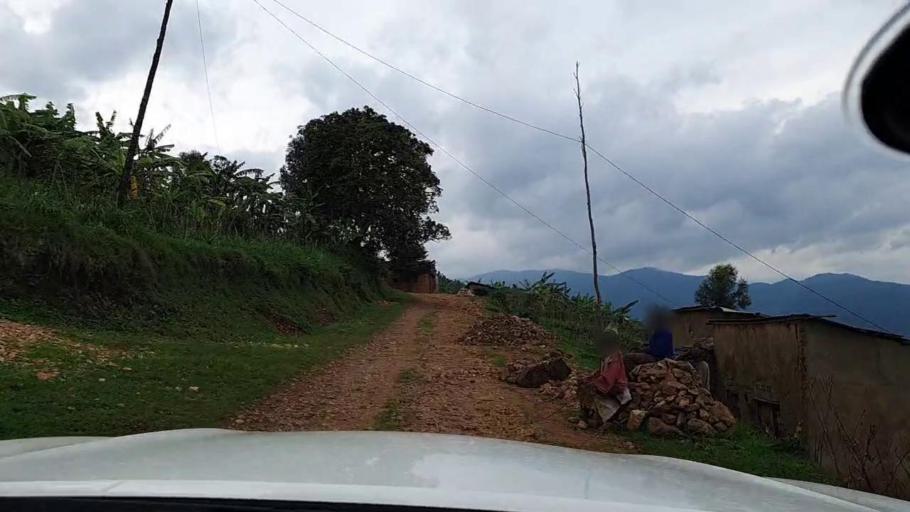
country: RW
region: Western Province
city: Kibuye
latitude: -2.1893
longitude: 29.2988
